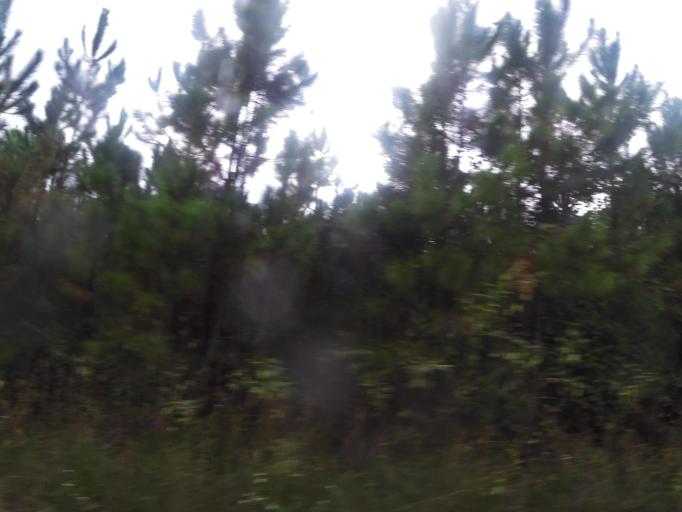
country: US
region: Florida
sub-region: Flagler County
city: Bunnell
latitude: 29.5407
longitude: -81.3226
